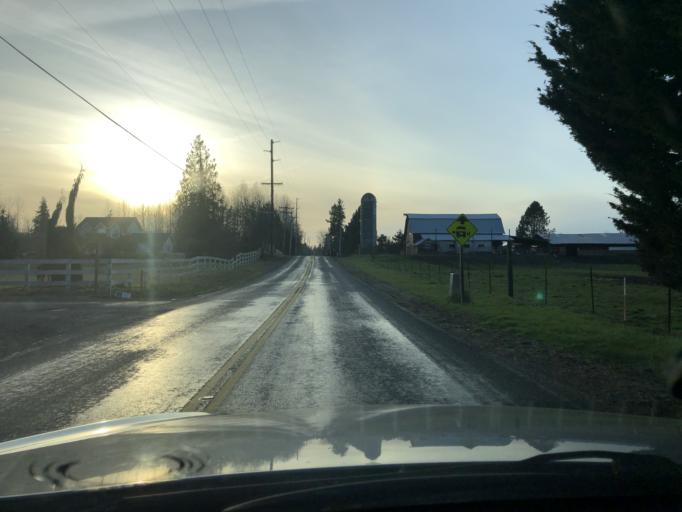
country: US
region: Washington
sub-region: Pierce County
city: Bonney Lake
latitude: 47.2211
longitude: -122.1259
